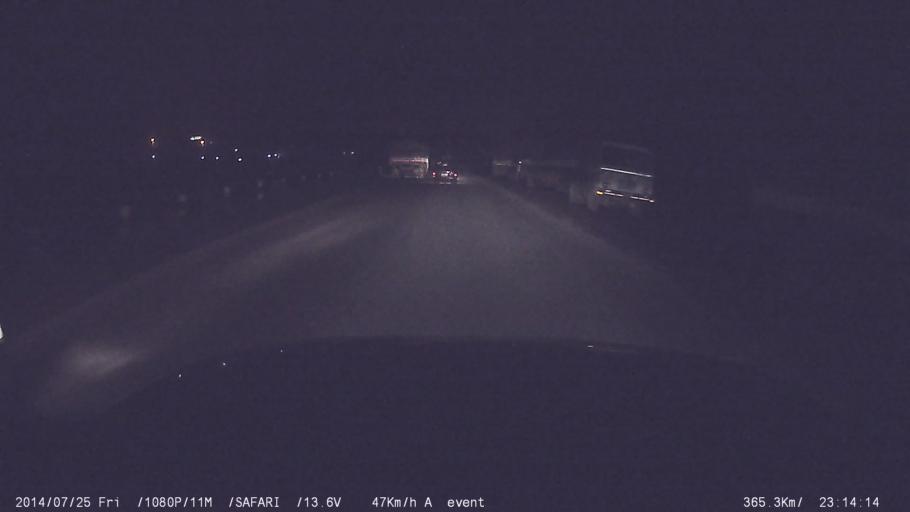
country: IN
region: Tamil Nadu
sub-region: Coimbatore
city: Madukkarai
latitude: 10.8944
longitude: 76.9308
